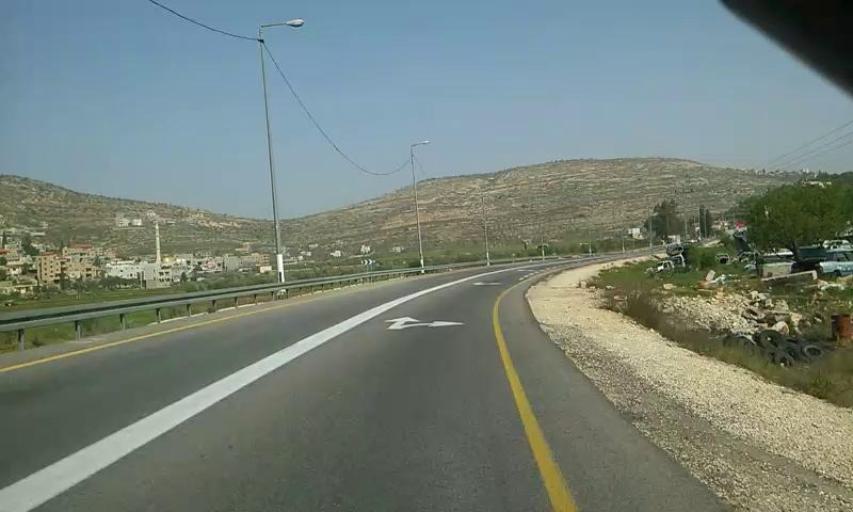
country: PS
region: West Bank
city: Al Lubban ash Sharqiyah
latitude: 32.0714
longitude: 35.2482
